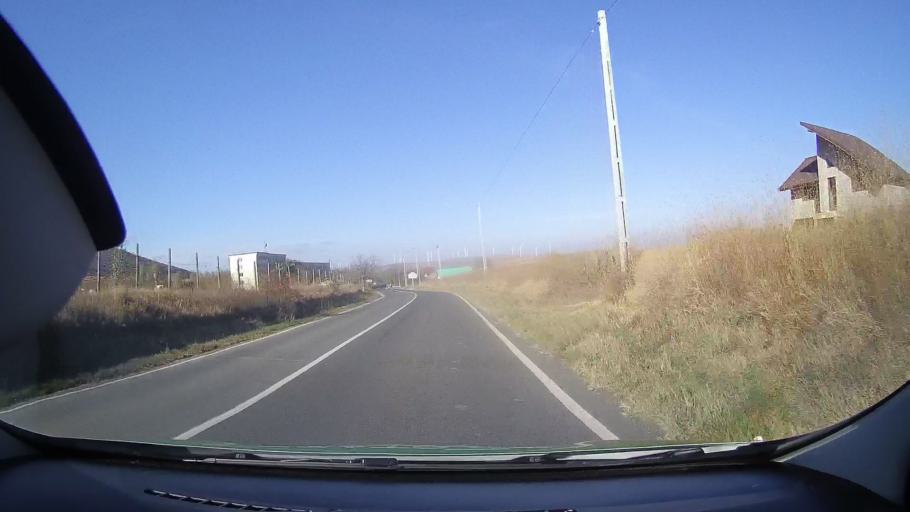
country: RO
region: Tulcea
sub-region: Oras Babadag
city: Babadag
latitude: 44.8844
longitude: 28.7389
